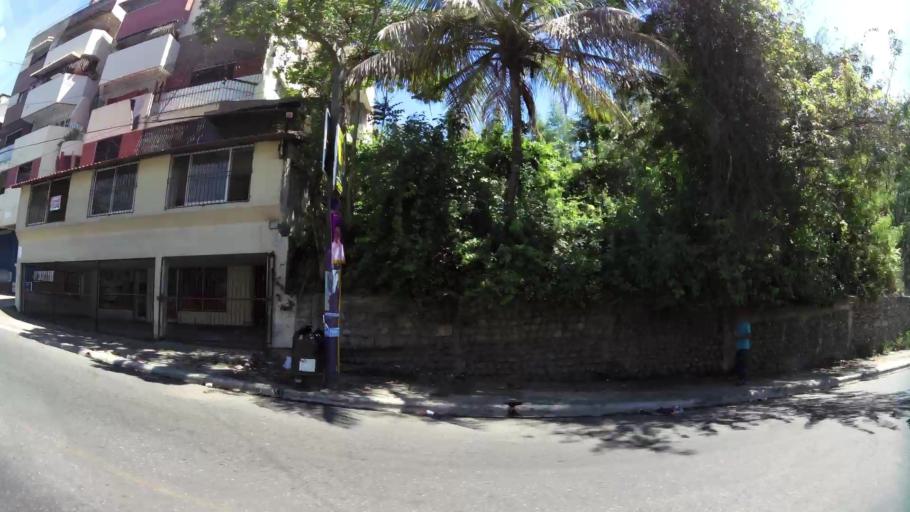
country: DO
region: Santiago
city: Santiago de los Caballeros
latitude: 19.4462
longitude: -70.6968
